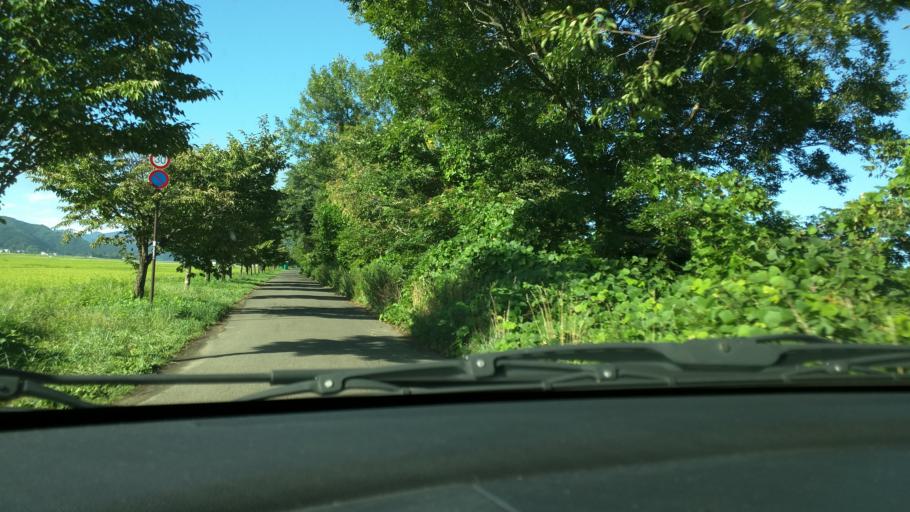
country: JP
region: Fukushima
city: Inawashiro
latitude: 37.4362
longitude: 140.1464
